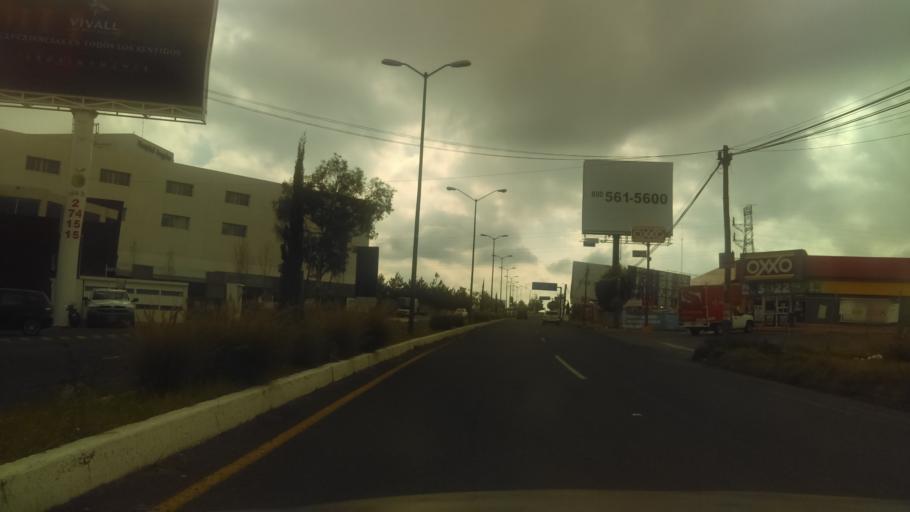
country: MX
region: Michoacan
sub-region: Morelia
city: Montana Monarca (Punta Altozano)
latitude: 19.6679
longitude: -101.1675
